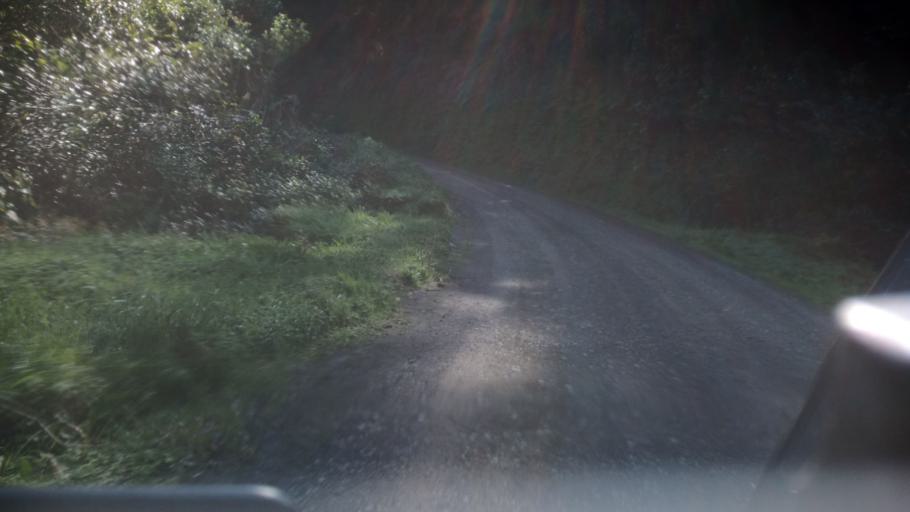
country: NZ
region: Bay of Plenty
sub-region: Opotiki District
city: Opotiki
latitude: -38.0514
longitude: 177.4552
